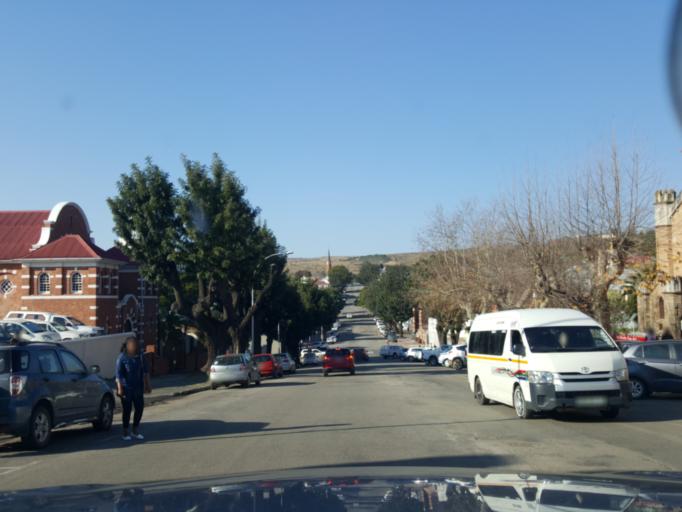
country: ZA
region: Eastern Cape
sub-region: Cacadu District Municipality
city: Grahamstown
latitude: -33.3108
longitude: 26.5270
